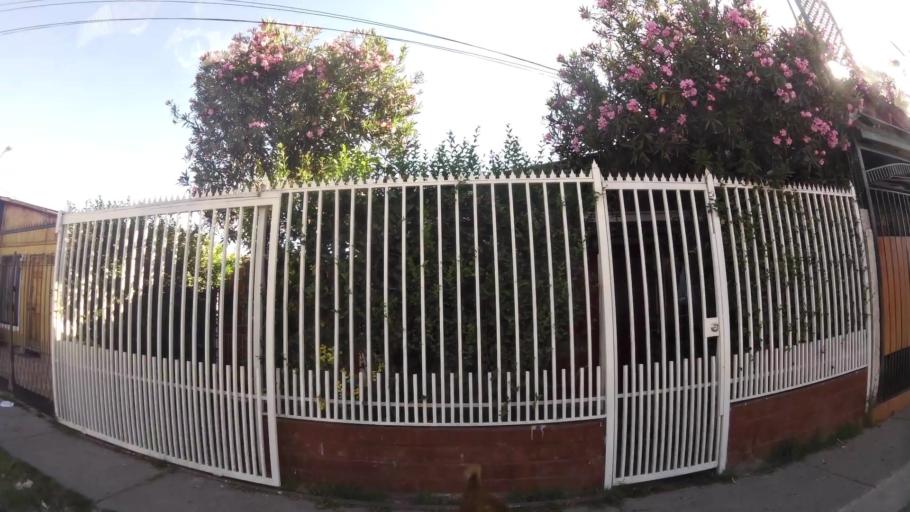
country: CL
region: Santiago Metropolitan
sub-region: Provincia de Maipo
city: San Bernardo
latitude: -33.6031
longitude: -70.6839
